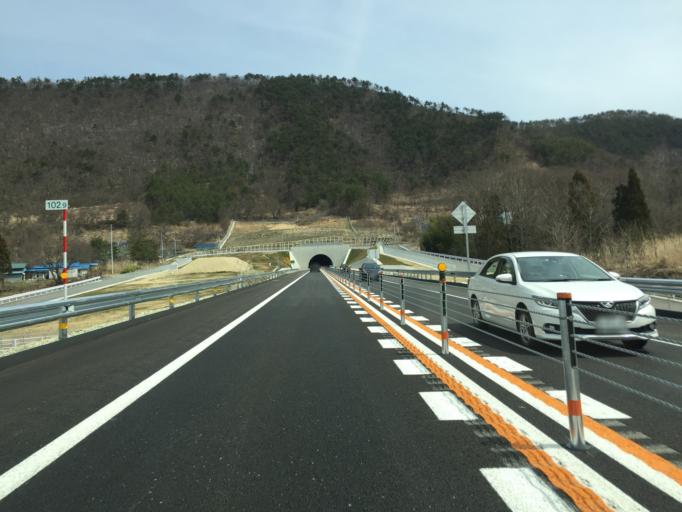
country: JP
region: Yamagata
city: Takahata
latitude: 38.0790
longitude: 140.1984
